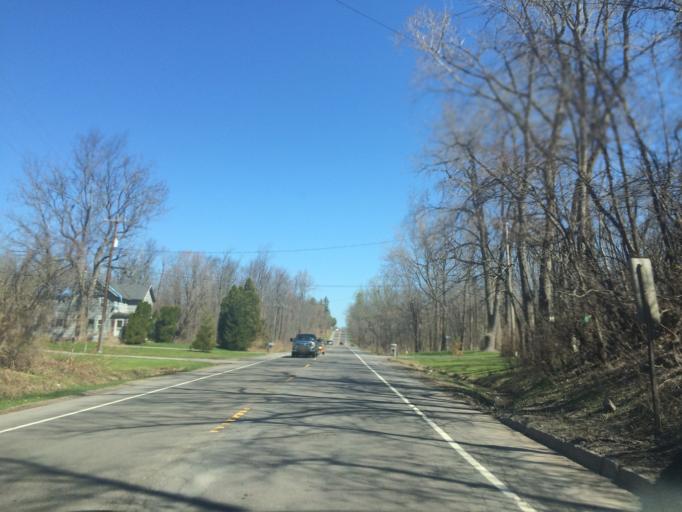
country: US
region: New York
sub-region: Wayne County
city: Macedon
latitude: 43.0829
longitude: -77.3015
